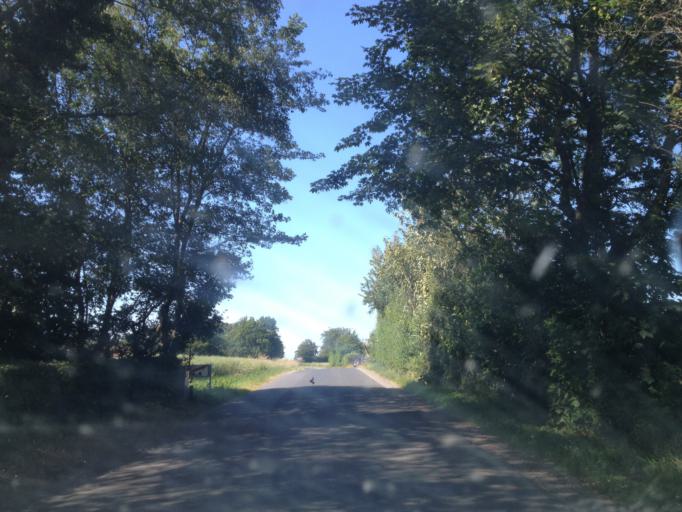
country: DK
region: South Denmark
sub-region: Kolding Kommune
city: Christiansfeld
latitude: 55.4011
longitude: 9.5176
